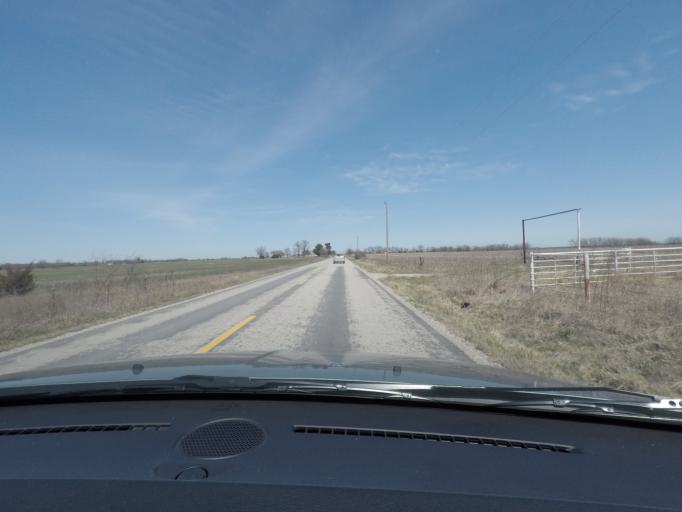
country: US
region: Kansas
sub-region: Lyon County
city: Emporia
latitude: 38.5425
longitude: -96.1700
